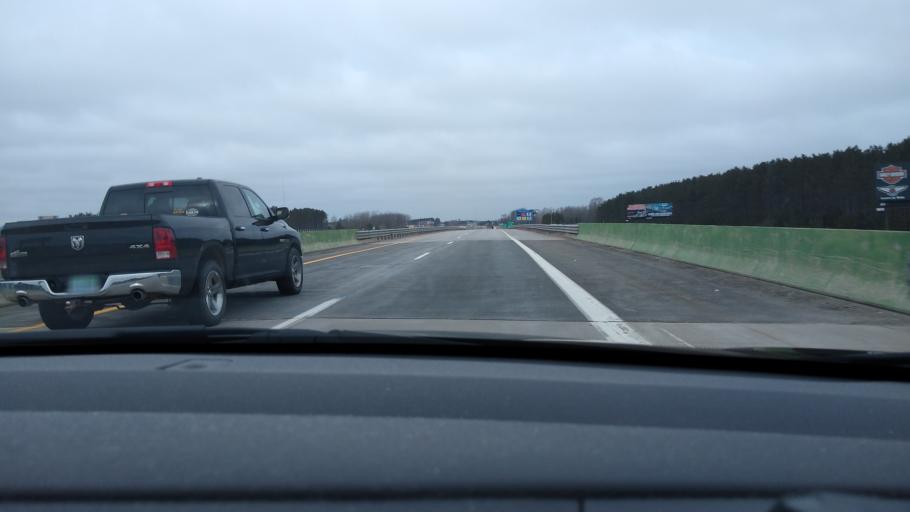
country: US
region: Michigan
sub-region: Otsego County
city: Gaylord
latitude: 45.0032
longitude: -84.6855
